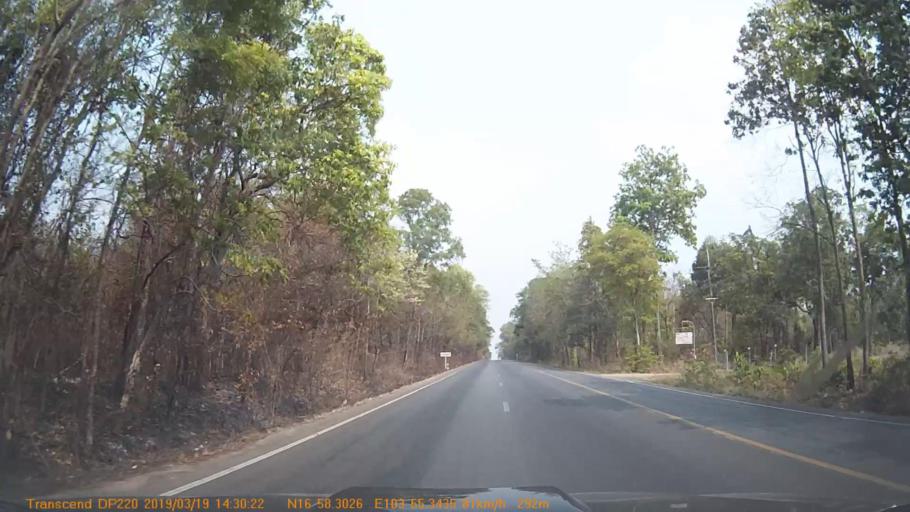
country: TH
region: Sakon Nakhon
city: Phu Phan
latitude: 16.9716
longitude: 103.9228
